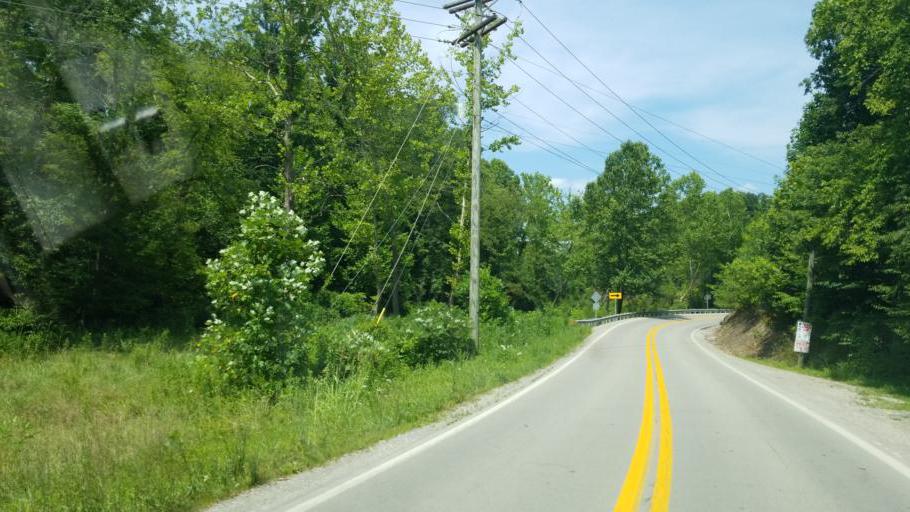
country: US
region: West Virginia
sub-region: Kanawha County
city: Nitro
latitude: 38.4520
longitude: -81.8785
